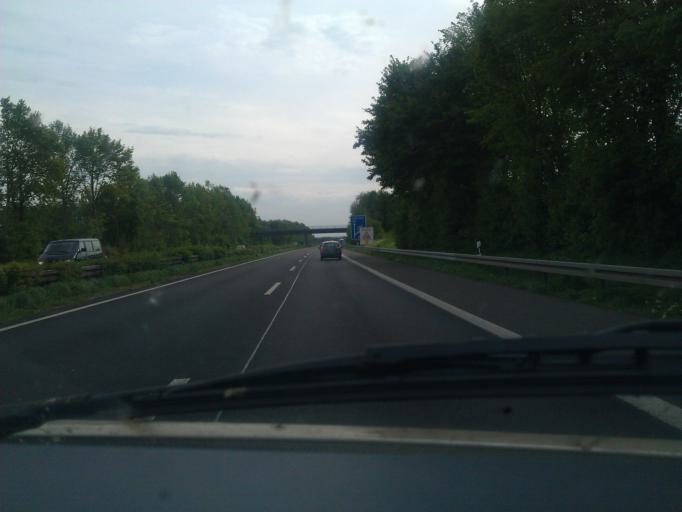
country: DE
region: North Rhine-Westphalia
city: Julich
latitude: 50.9715
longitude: 6.3702
